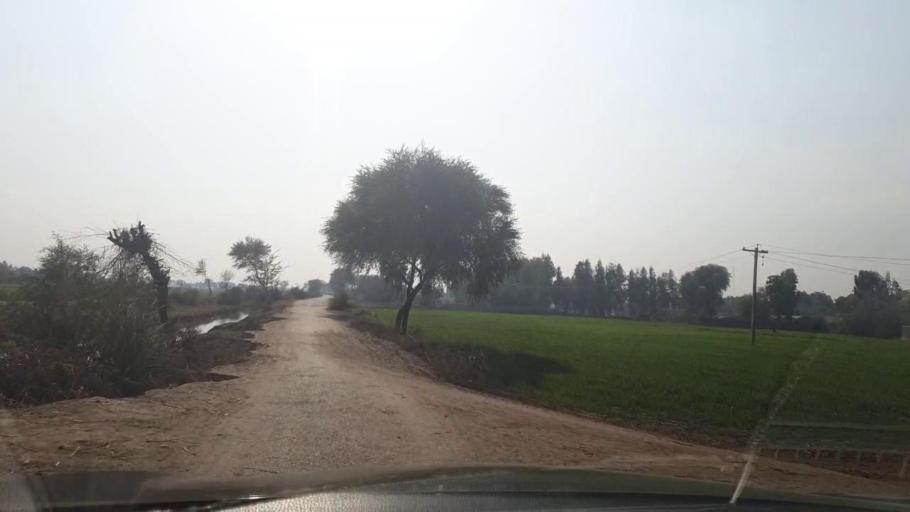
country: PK
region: Sindh
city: Khairpur
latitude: 28.1167
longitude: 69.6406
